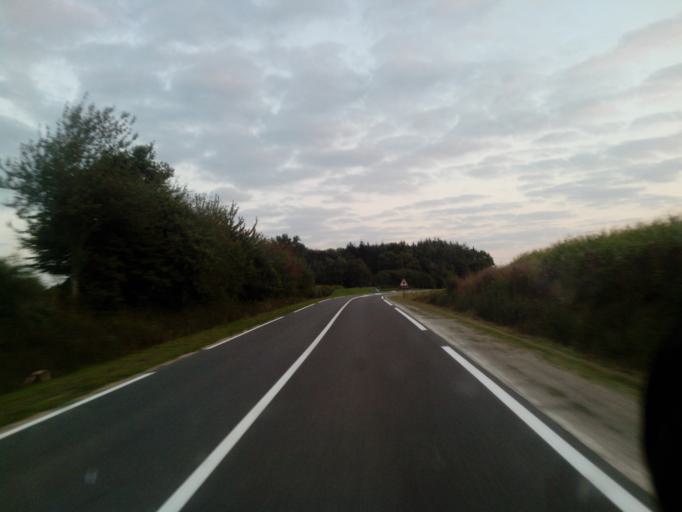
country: FR
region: Brittany
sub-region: Departement d'Ille-et-Vilaine
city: Bedee
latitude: 48.1617
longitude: -1.9455
